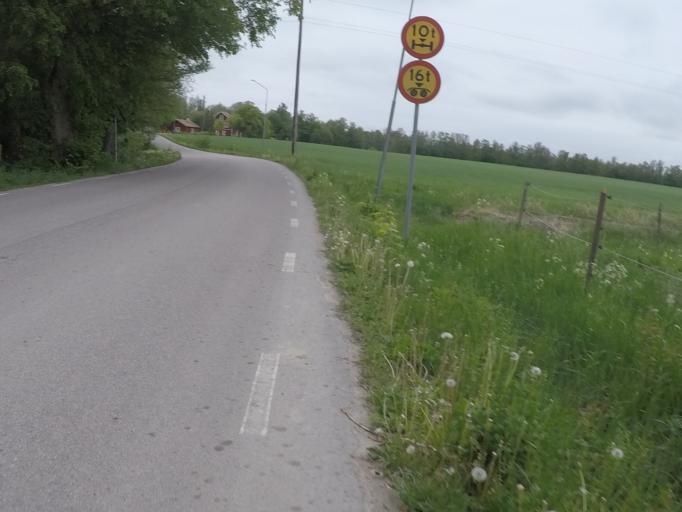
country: SE
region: Vaestmanland
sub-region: Hallstahammars Kommun
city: Kolback
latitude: 59.5502
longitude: 16.2575
